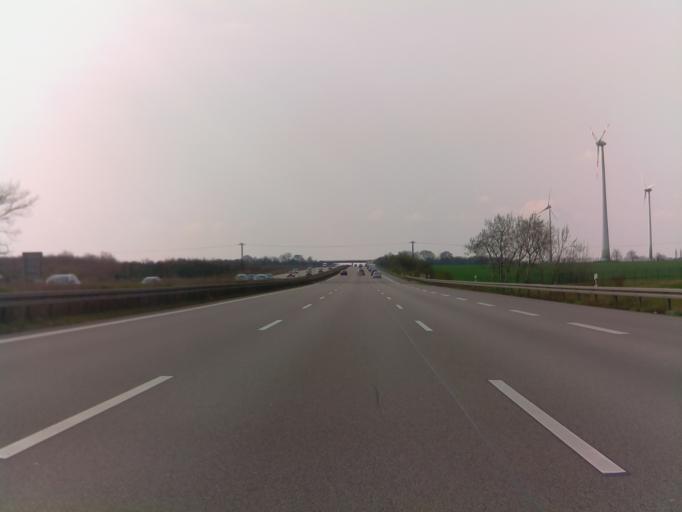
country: DE
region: Saxony
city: Grosslehna
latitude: 51.3225
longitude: 12.1687
